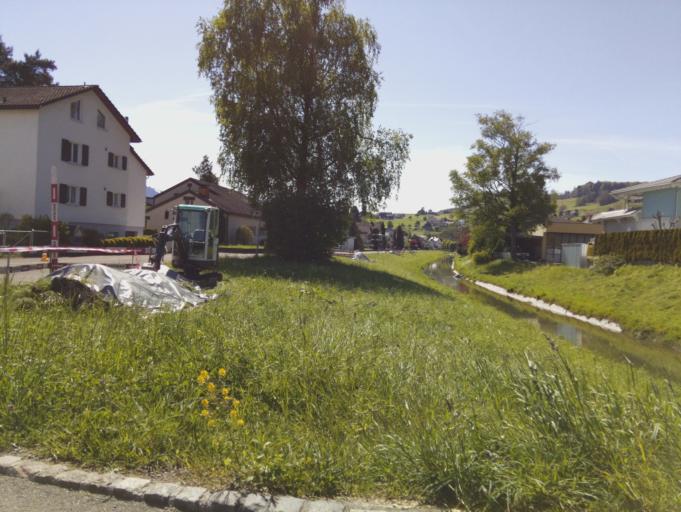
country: CH
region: Schwyz
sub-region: Bezirk March
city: Tuggen
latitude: 47.2034
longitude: 8.9491
